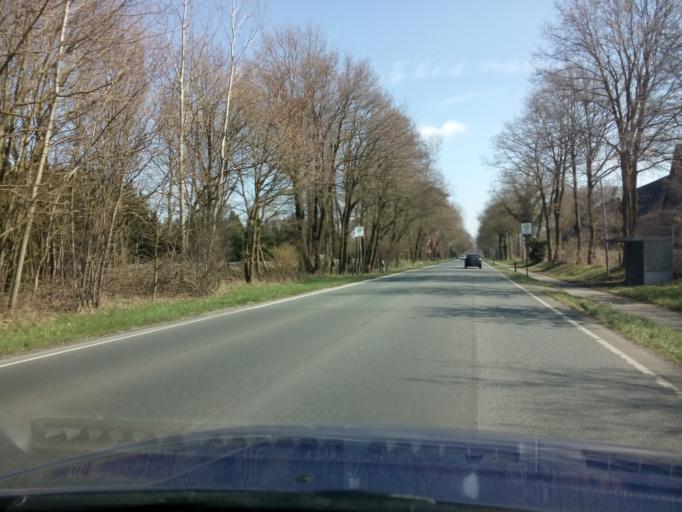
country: DE
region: Lower Saxony
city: Emlichheim
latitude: 52.6104
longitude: 6.8259
